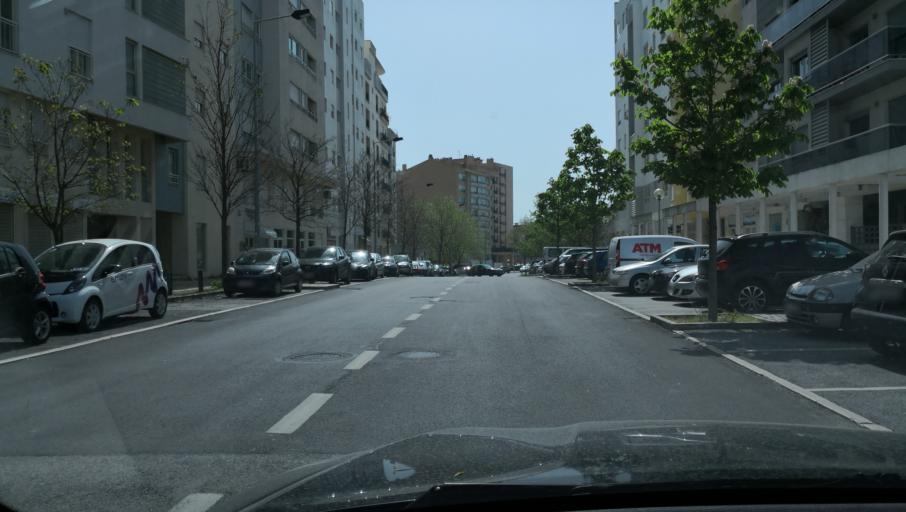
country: PT
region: Lisbon
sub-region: Odivelas
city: Olival do Basto
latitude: 38.7699
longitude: -9.1697
